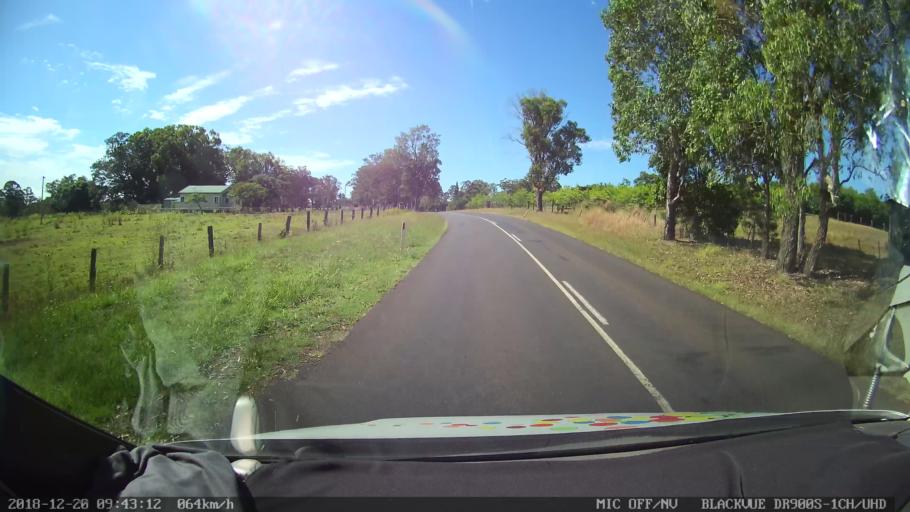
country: AU
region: New South Wales
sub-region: Lismore Municipality
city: Lismore
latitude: -28.7237
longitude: 153.2952
